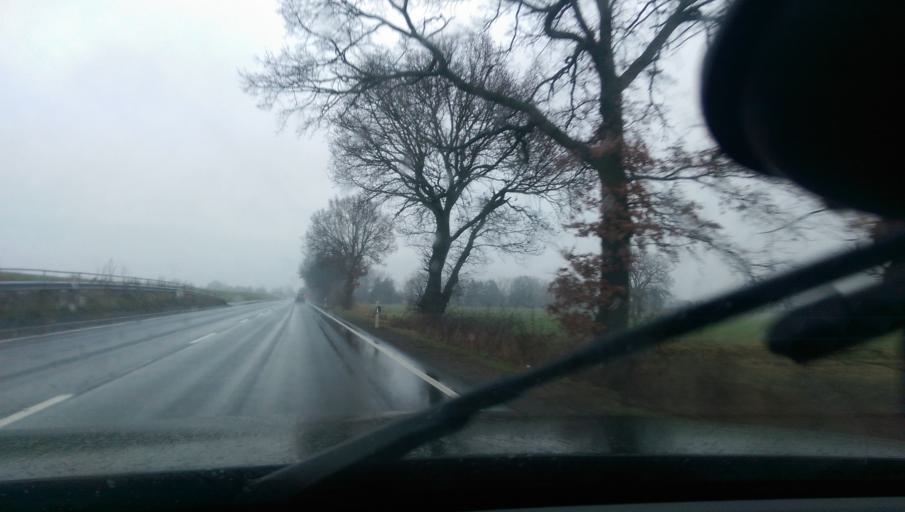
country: DE
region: Lower Saxony
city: Dorverden
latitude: 52.8675
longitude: 9.2325
